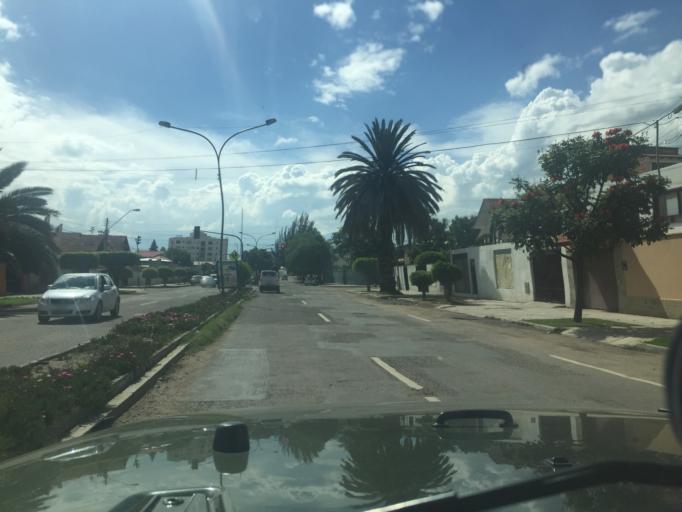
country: BO
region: Cochabamba
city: Cochabamba
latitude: -17.3784
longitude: -66.1668
